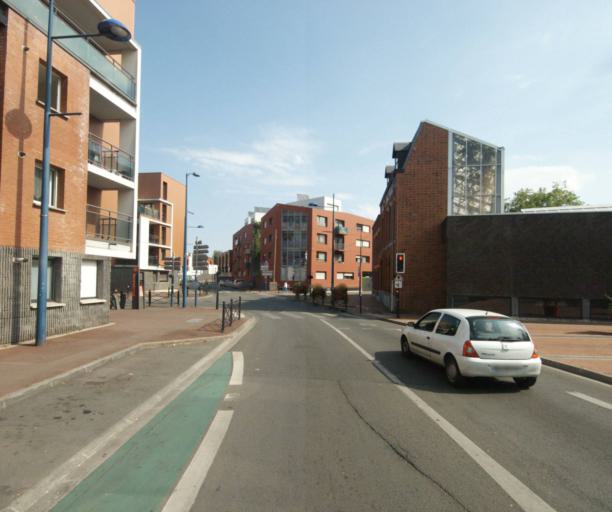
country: FR
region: Nord-Pas-de-Calais
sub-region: Departement du Nord
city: Tourcoing
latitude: 50.7244
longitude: 3.1662
